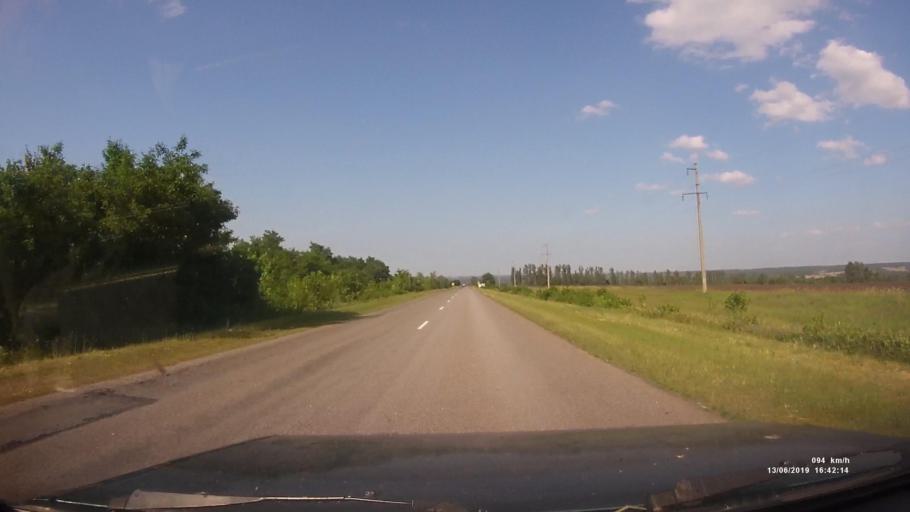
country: RU
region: Rostov
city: Kazanskaya
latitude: 49.9409
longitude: 41.3998
